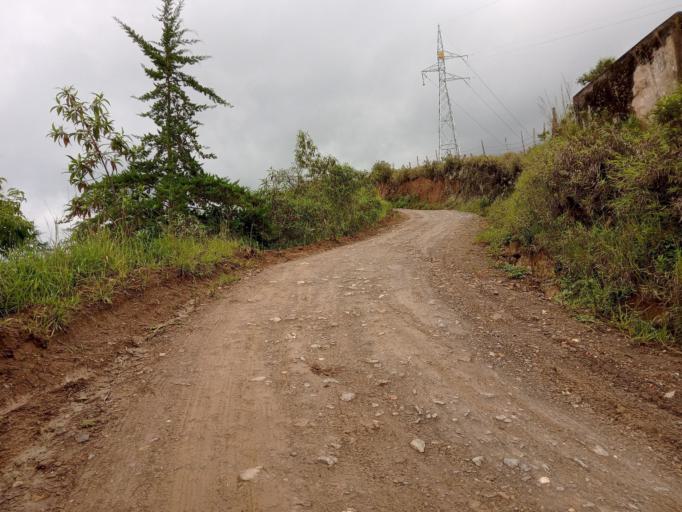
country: CO
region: Cundinamarca
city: Tenza
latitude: 5.0778
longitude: -73.4355
